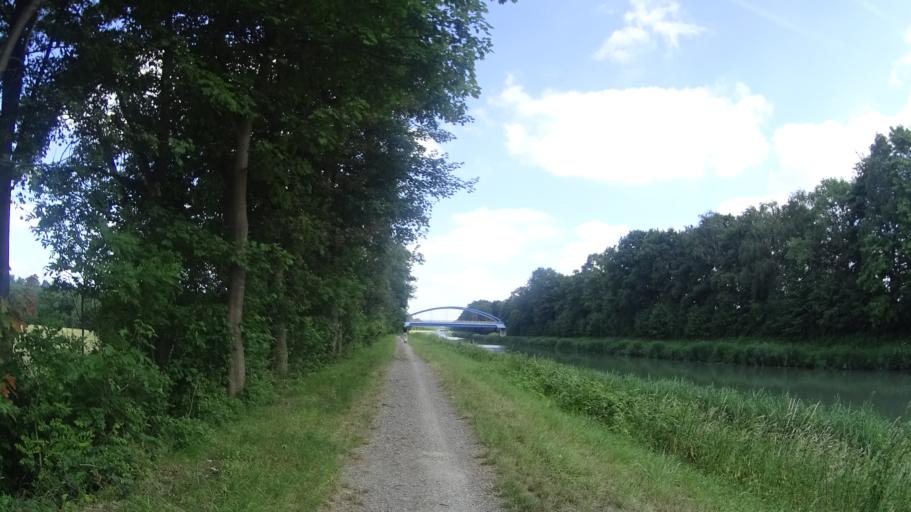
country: DE
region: Lower Saxony
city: Algermissen
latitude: 52.2493
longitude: 9.9511
